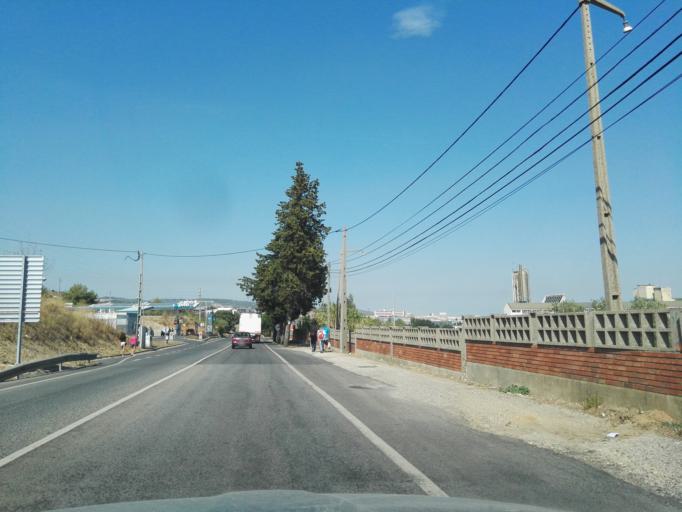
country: PT
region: Lisbon
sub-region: Vila Franca de Xira
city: Vialonga
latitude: 38.8783
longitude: -9.0517
